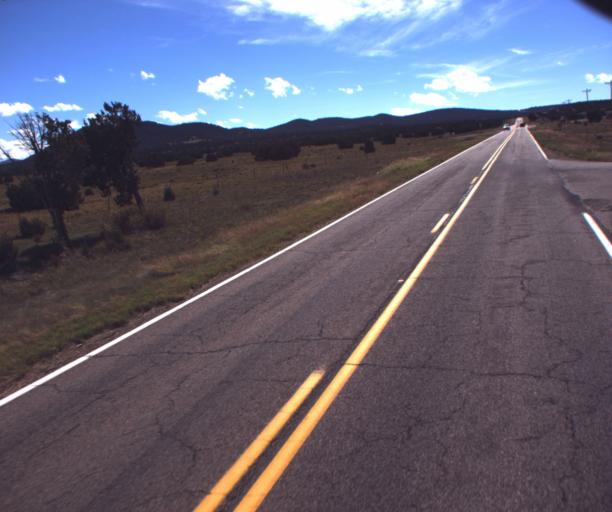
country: US
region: Arizona
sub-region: Navajo County
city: White Mountain Lake
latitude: 34.3382
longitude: -109.7362
